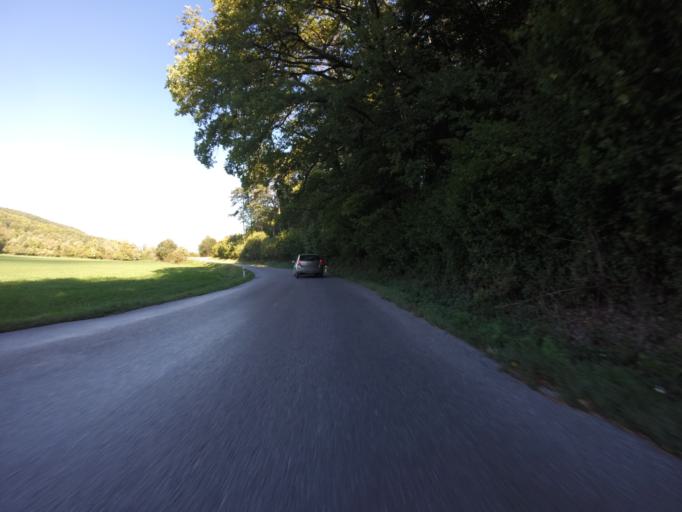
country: SK
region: Nitriansky
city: Ilava
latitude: 48.9890
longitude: 18.2746
